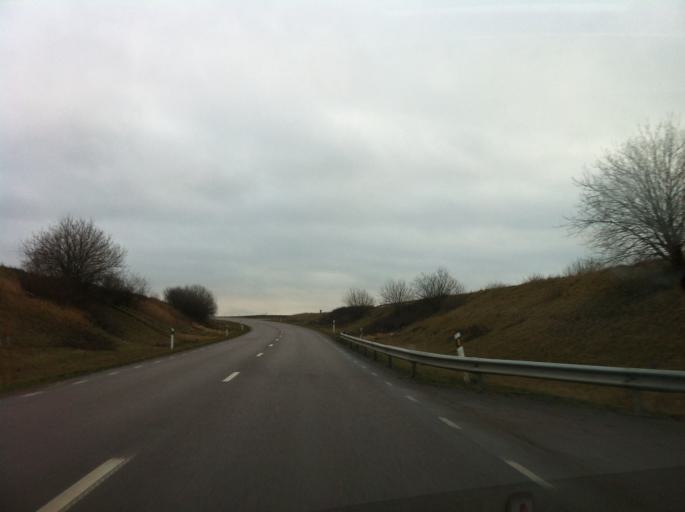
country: SE
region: Skane
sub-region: Helsingborg
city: Glumslov
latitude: 55.9575
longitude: 12.7938
